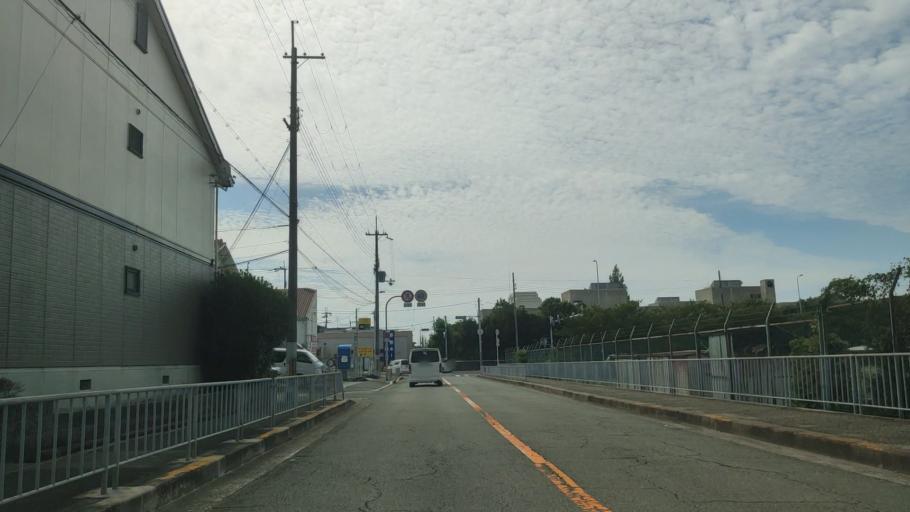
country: JP
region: Osaka
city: Ikeda
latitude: 34.8117
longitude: 135.4350
